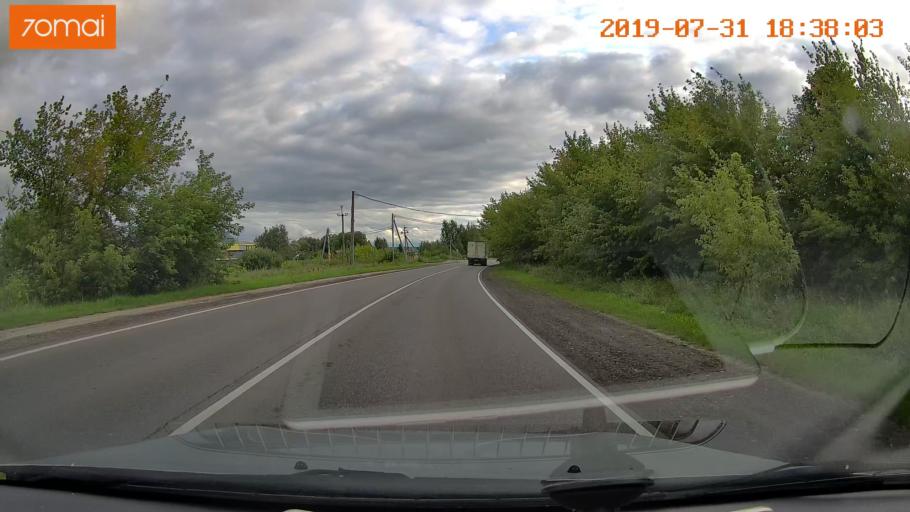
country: RU
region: Moskovskaya
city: Voskresensk
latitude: 55.2742
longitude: 38.6581
